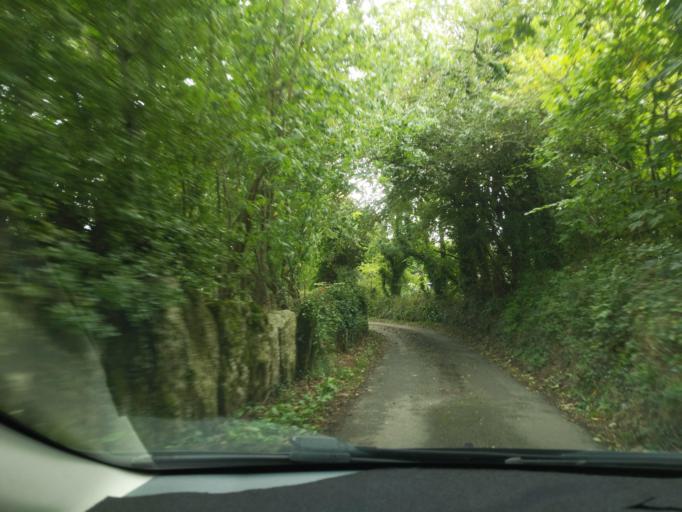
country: GB
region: England
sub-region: Cornwall
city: Lostwithiel
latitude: 50.3933
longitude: -4.7049
